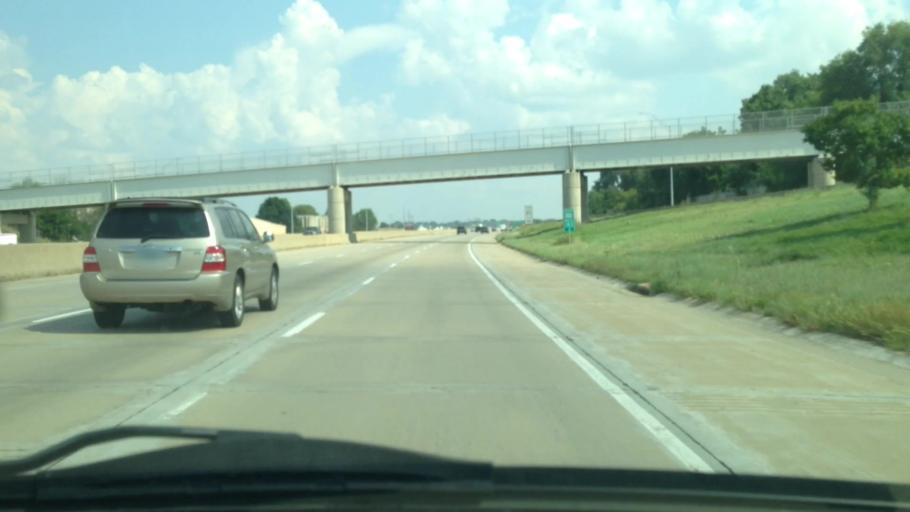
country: US
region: Iowa
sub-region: Black Hawk County
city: Waterloo
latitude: 42.5079
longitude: -92.3745
